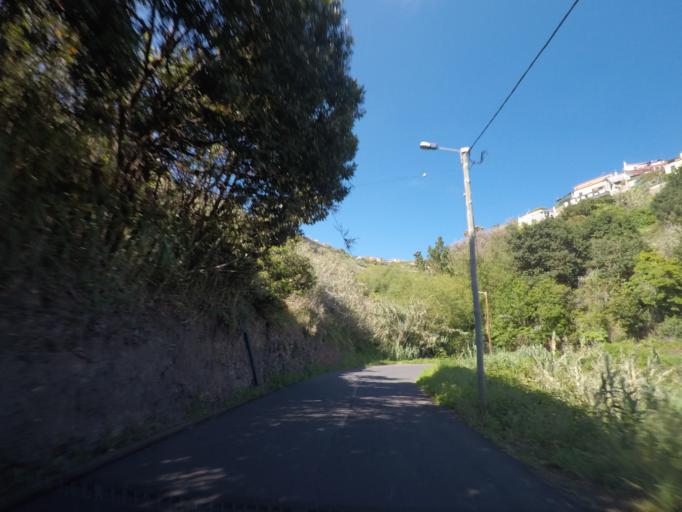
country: PT
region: Madeira
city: Ponta do Sol
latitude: 32.6968
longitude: -17.1011
